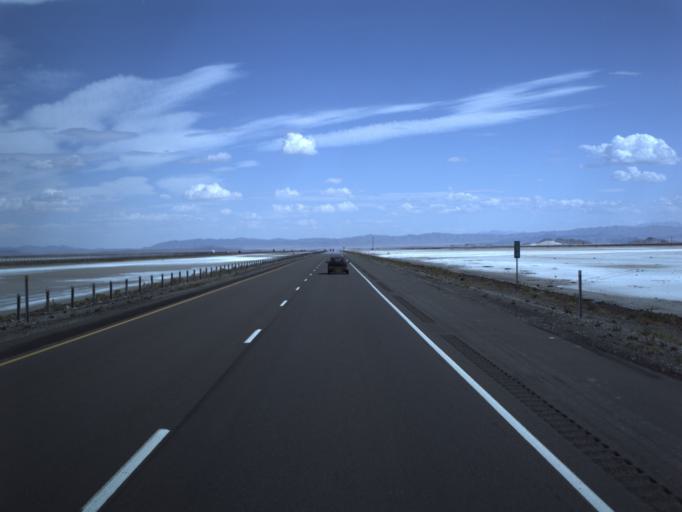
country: US
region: Utah
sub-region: Tooele County
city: Wendover
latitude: 40.7285
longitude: -113.3982
